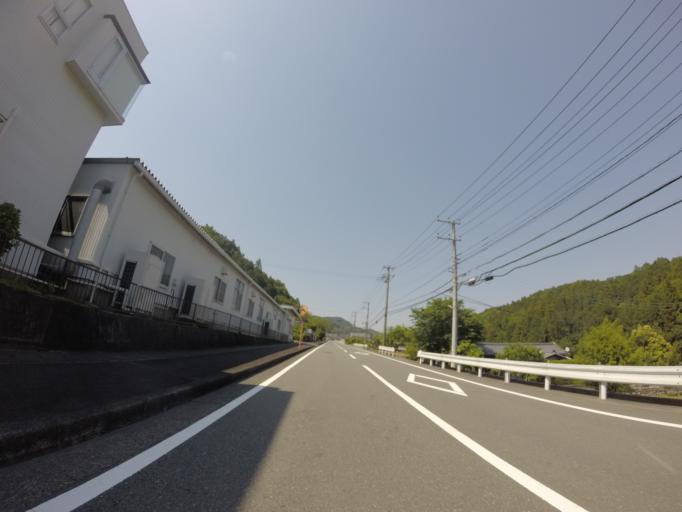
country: JP
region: Shizuoka
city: Fujinomiya
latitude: 35.2052
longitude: 138.5870
